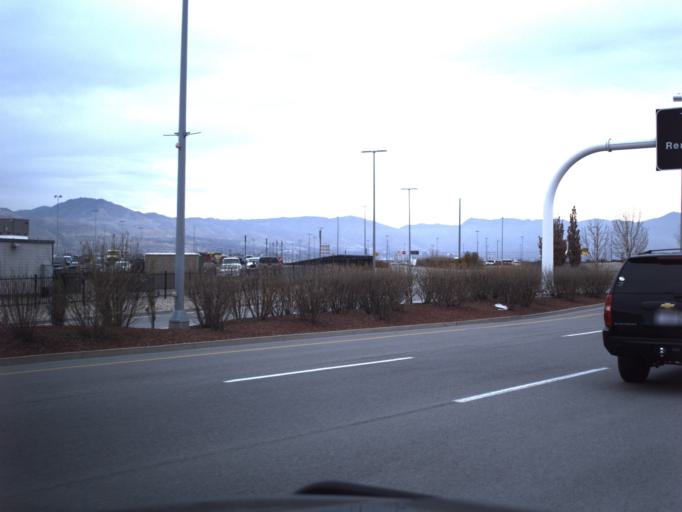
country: US
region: Utah
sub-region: Salt Lake County
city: West Valley City
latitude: 40.7753
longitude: -111.9888
